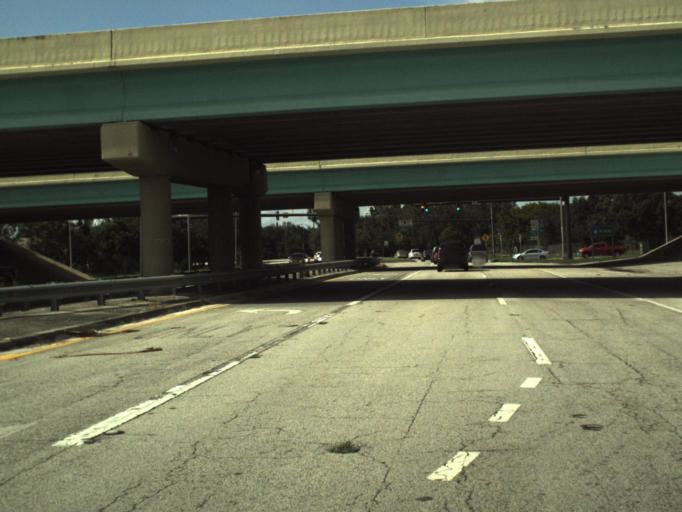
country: US
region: Florida
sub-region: Broward County
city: Parkland
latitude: 26.3015
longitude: -80.2505
